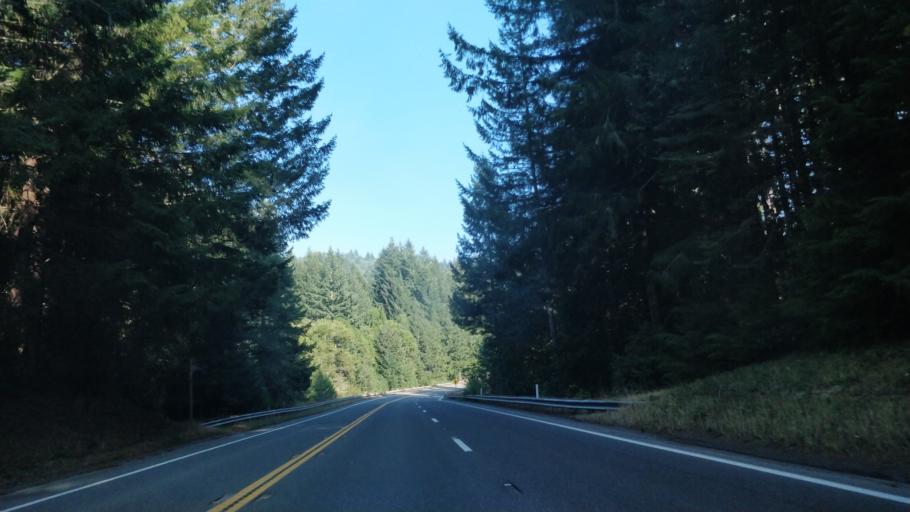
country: US
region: California
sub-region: Humboldt County
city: Blue Lake
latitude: 40.9456
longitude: -123.8782
